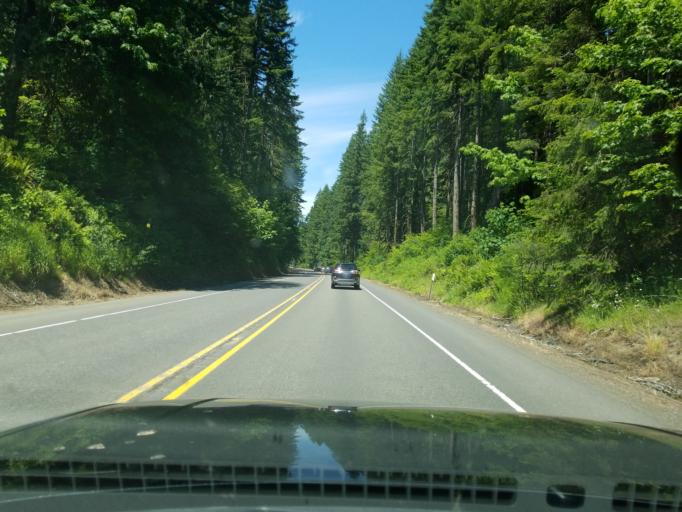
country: US
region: Oregon
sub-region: Columbia County
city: Vernonia
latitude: 45.7726
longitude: -123.3234
